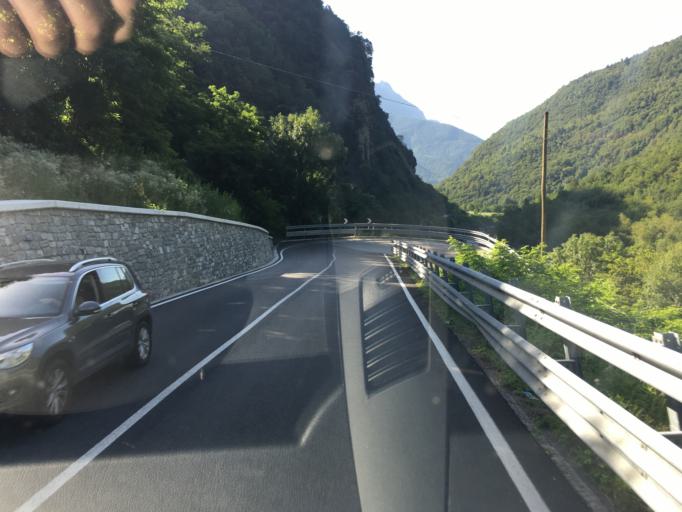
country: IT
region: Lombardy
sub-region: Provincia di Sondrio
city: San Giacomo Filippo
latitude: 46.3348
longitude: 9.3706
